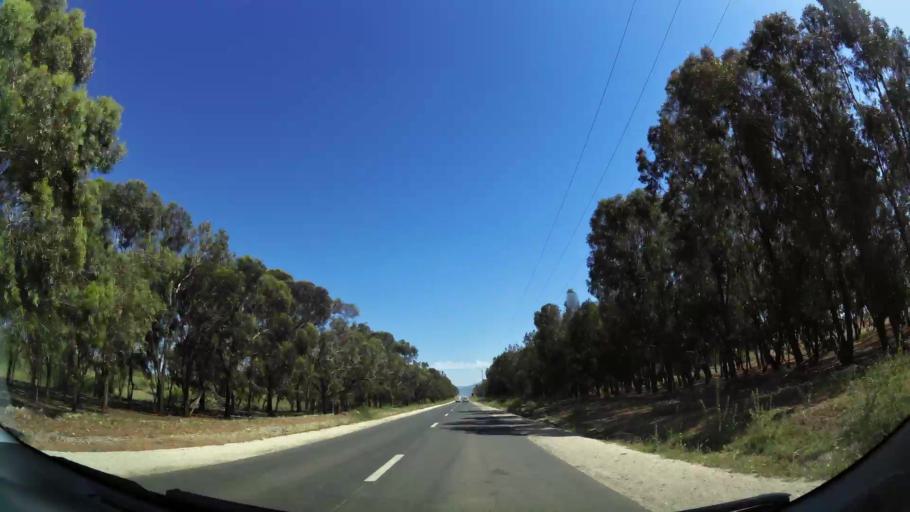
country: MA
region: Oriental
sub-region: Berkane-Taourirt
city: Madagh
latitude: 35.0021
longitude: -2.3963
